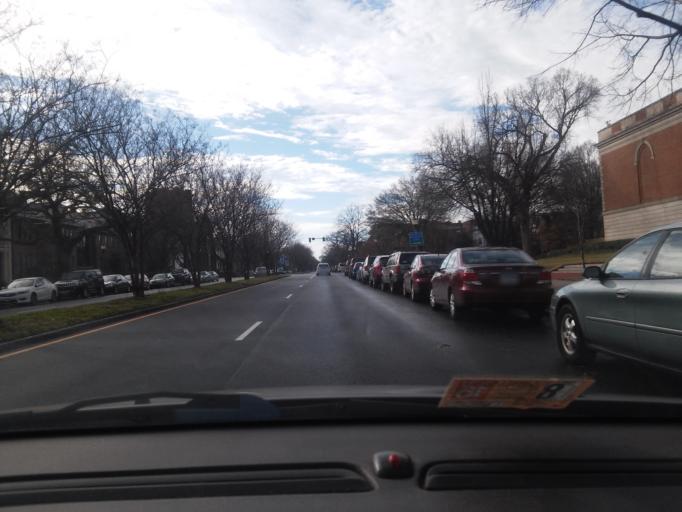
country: US
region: Virginia
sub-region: City of Richmond
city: Richmond
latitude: 37.5557
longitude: -77.4740
